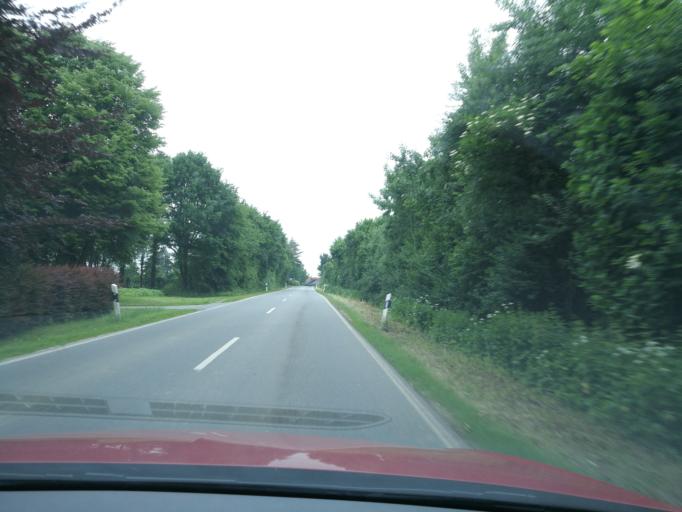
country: DE
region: Schleswig-Holstein
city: Politz
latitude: 53.7676
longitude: 10.3830
